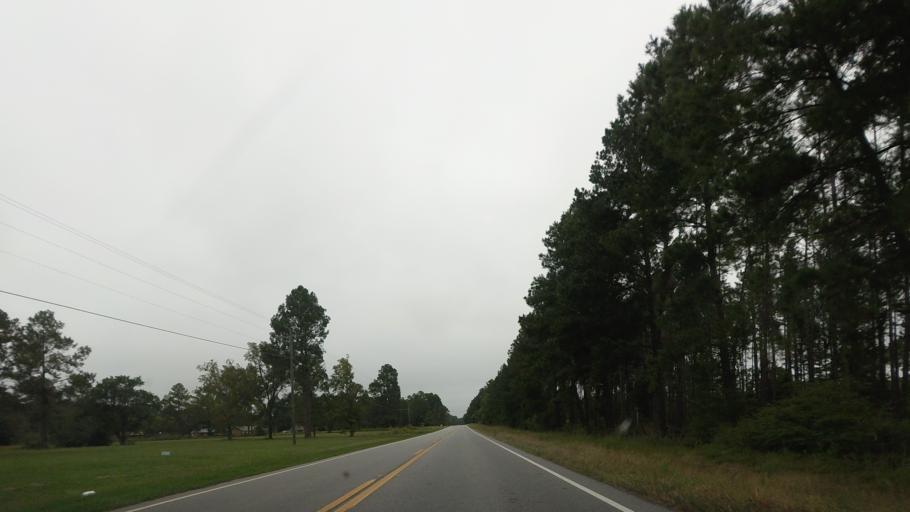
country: US
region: Georgia
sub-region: Berrien County
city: Nashville
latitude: 31.2393
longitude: -83.2450
